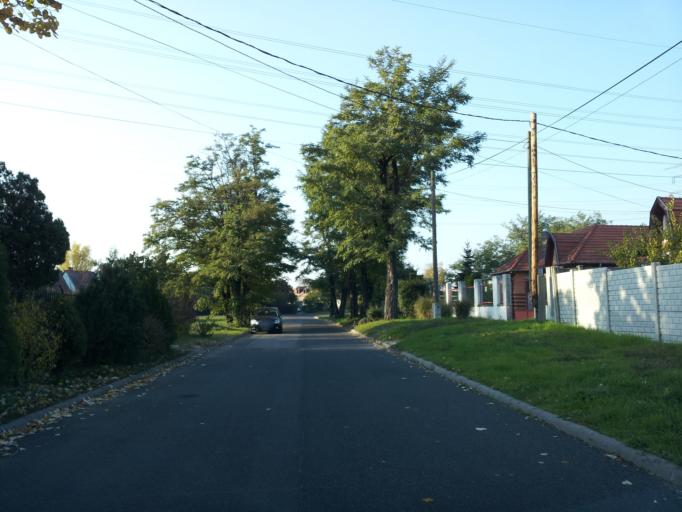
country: HU
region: Budapest
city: Budapest X. keruelet
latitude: 47.4723
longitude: 19.1684
